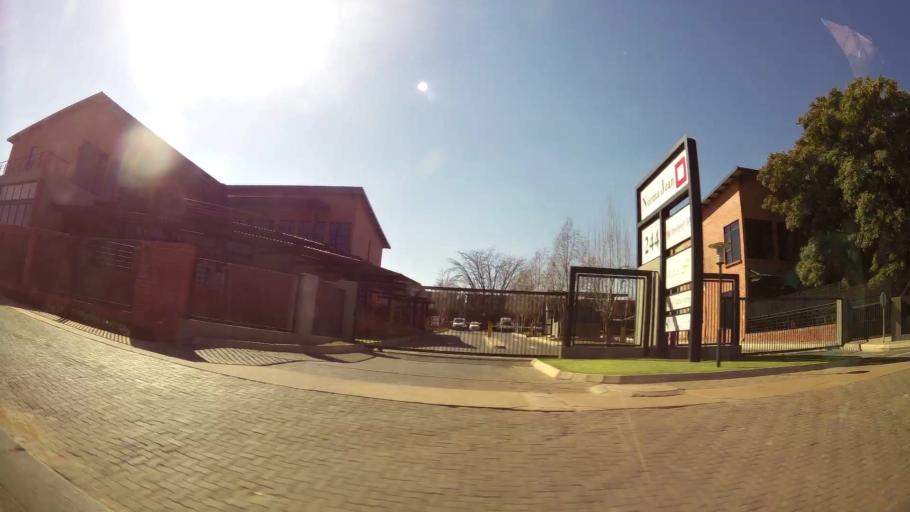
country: ZA
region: Gauteng
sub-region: City of Tshwane Metropolitan Municipality
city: Centurion
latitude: -25.8425
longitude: 28.1889
